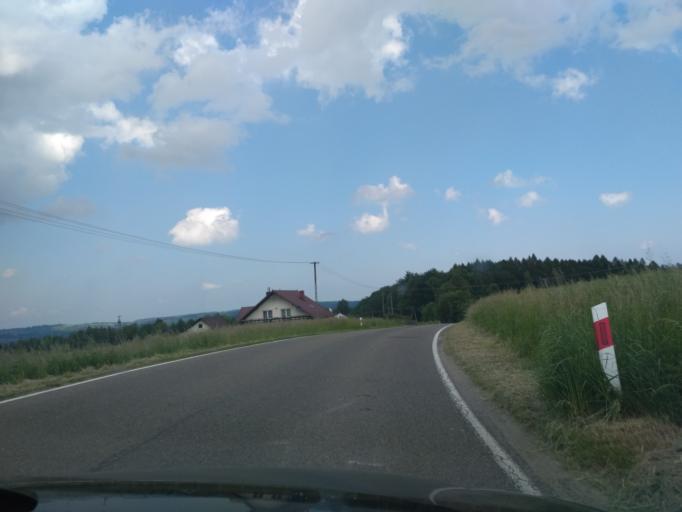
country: PL
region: Subcarpathian Voivodeship
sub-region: Powiat rzeszowski
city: Hyzne
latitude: 49.9387
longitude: 22.1892
